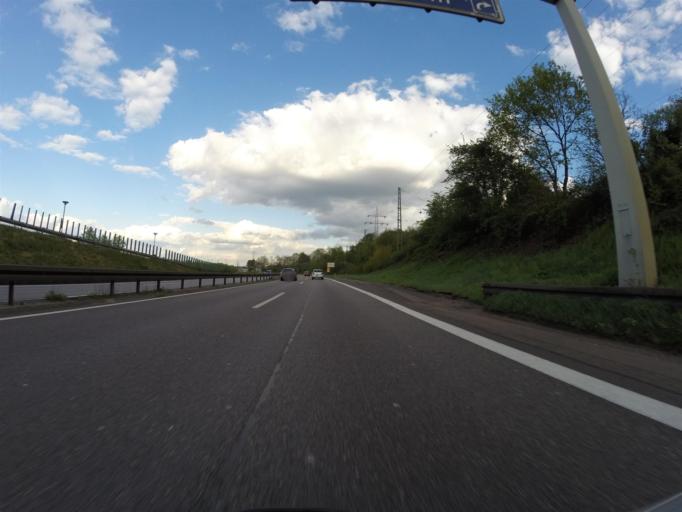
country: FR
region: Lorraine
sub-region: Departement de la Moselle
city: Schoeneck
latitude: 49.2395
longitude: 6.9290
